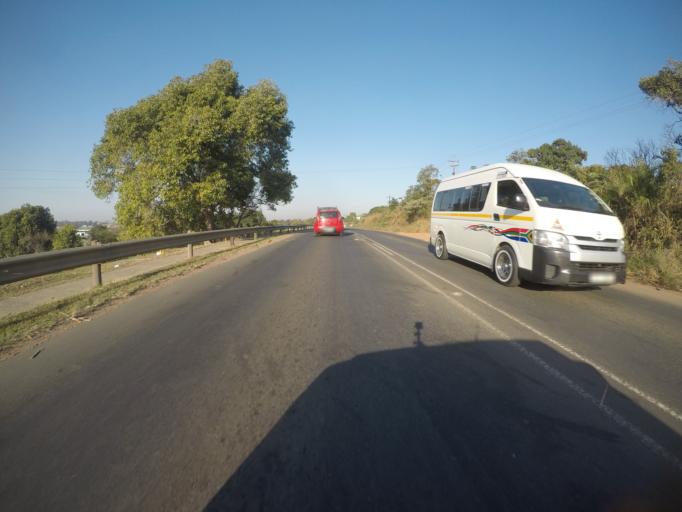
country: ZA
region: KwaZulu-Natal
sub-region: iLembe District Municipality
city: Stanger
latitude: -29.4057
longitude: 31.2490
